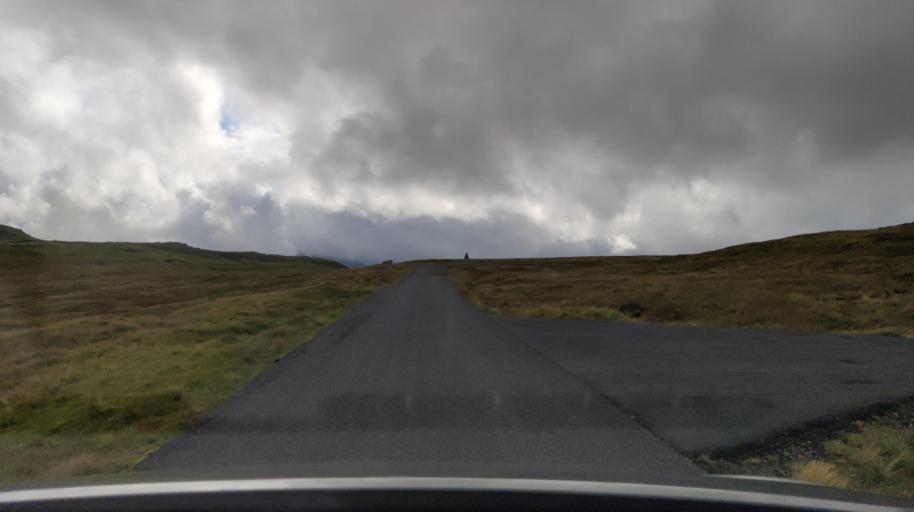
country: FO
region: Streymoy
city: Vestmanna
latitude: 62.1695
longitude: -7.1634
